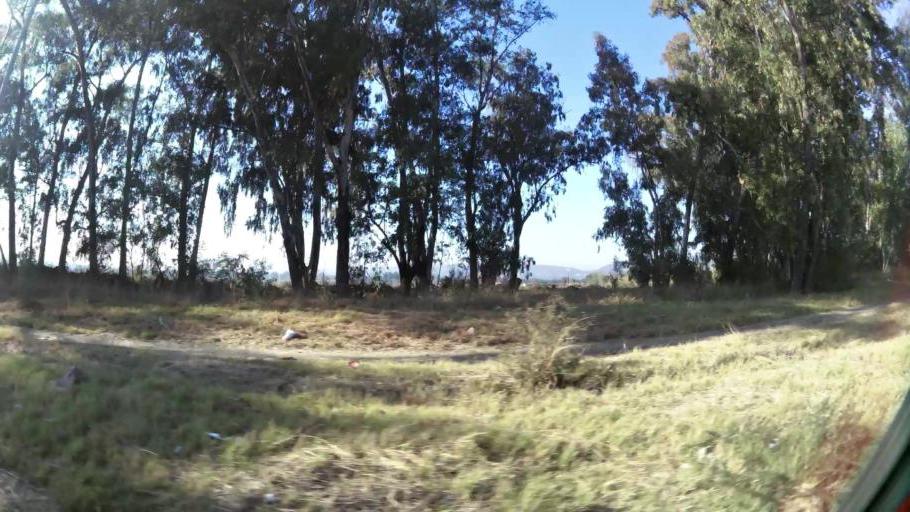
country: ZA
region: Gauteng
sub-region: City of Tshwane Metropolitan Municipality
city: Pretoria
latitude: -25.6610
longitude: 28.1843
